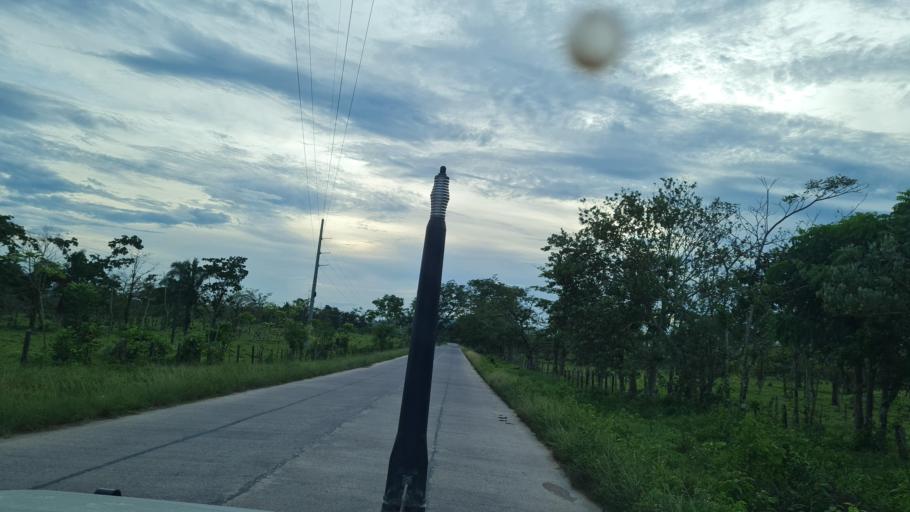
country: NI
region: Atlantico Norte (RAAN)
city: Siuna
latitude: 13.6833
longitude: -84.5861
